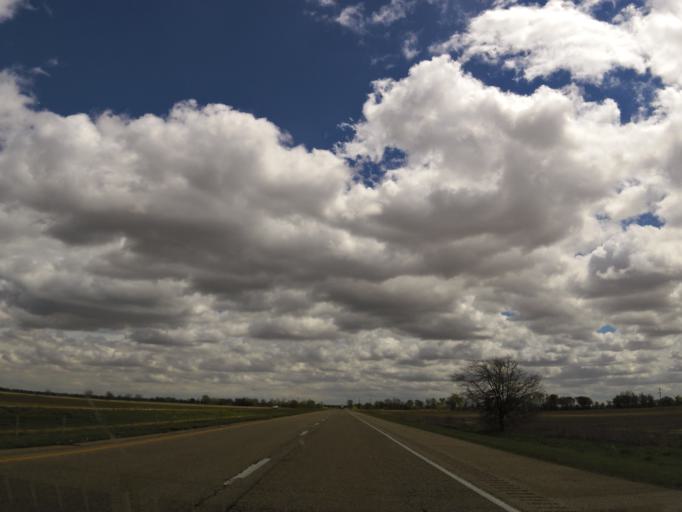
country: US
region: Arkansas
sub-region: Poinsett County
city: Trumann
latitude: 35.6527
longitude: -90.5318
